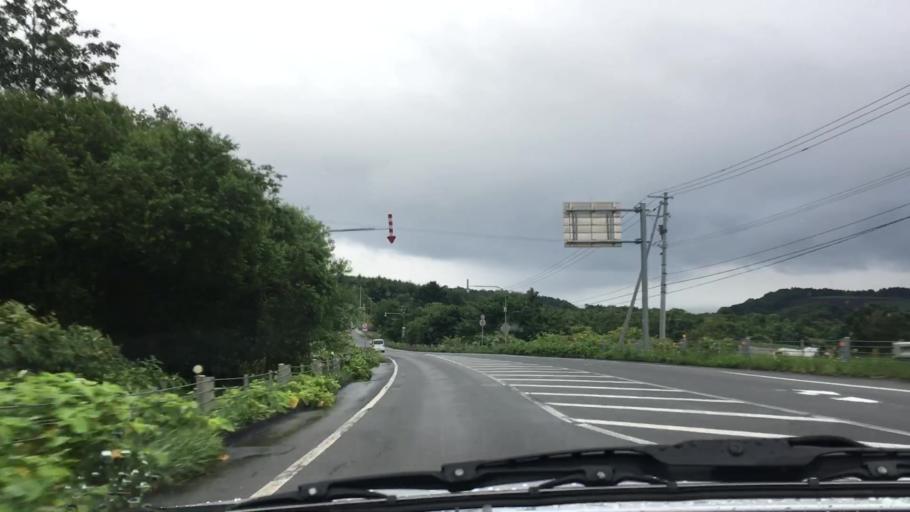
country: JP
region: Hokkaido
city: Niseko Town
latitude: 42.6052
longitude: 140.7269
